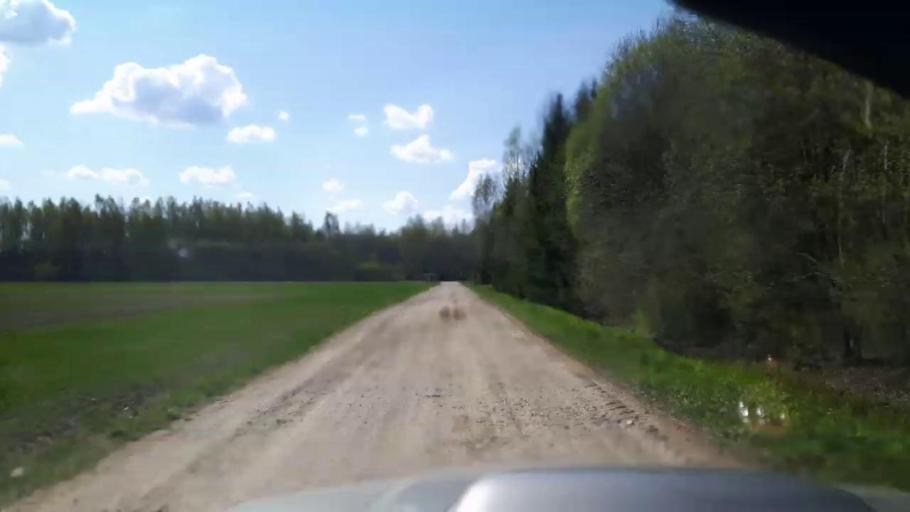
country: EE
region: Paernumaa
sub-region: Tootsi vald
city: Tootsi
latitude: 58.4920
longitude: 24.9428
